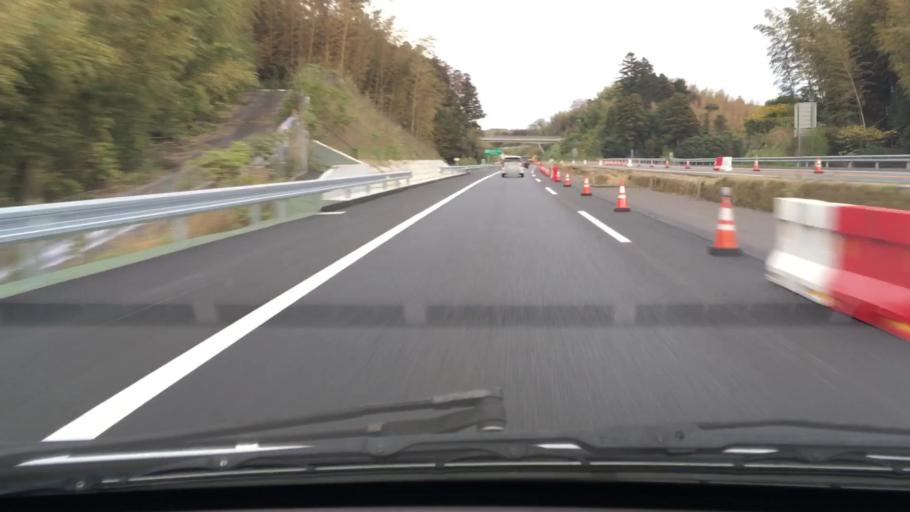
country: JP
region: Chiba
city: Kimitsu
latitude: 35.2975
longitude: 139.9357
